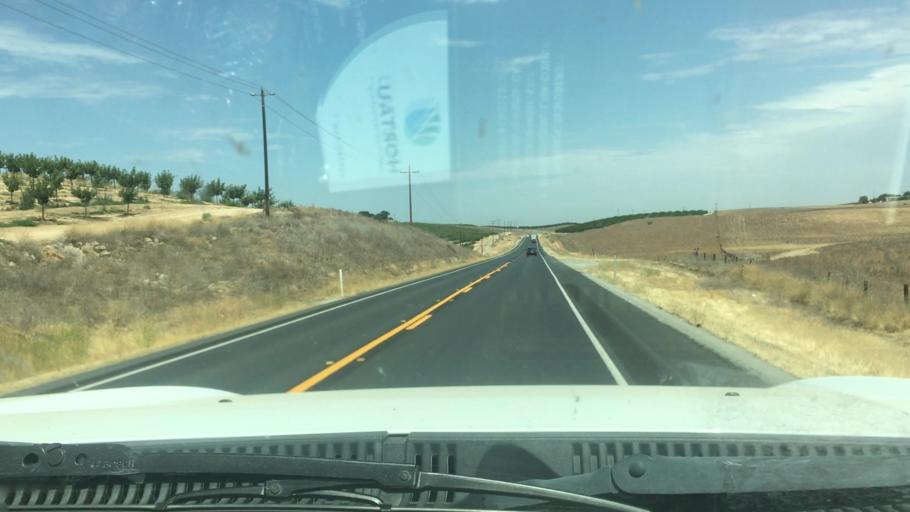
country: US
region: California
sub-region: Tulare County
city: Richgrove
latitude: 35.7050
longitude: -119.0629
